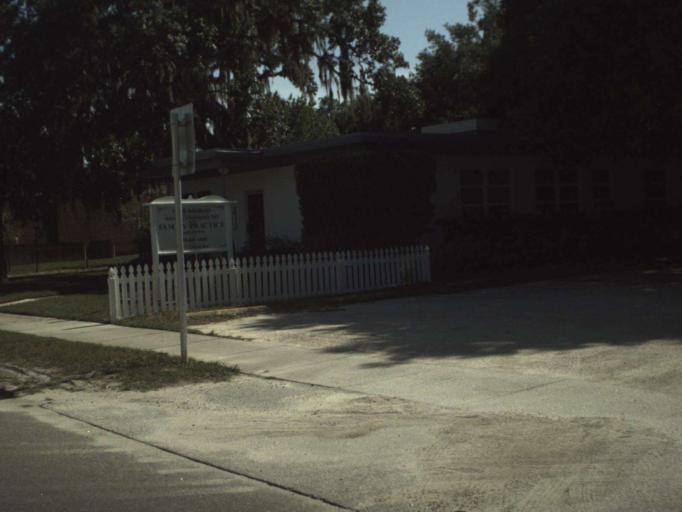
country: US
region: Florida
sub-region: Seminole County
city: Oviedo
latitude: 28.6695
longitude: -81.2085
